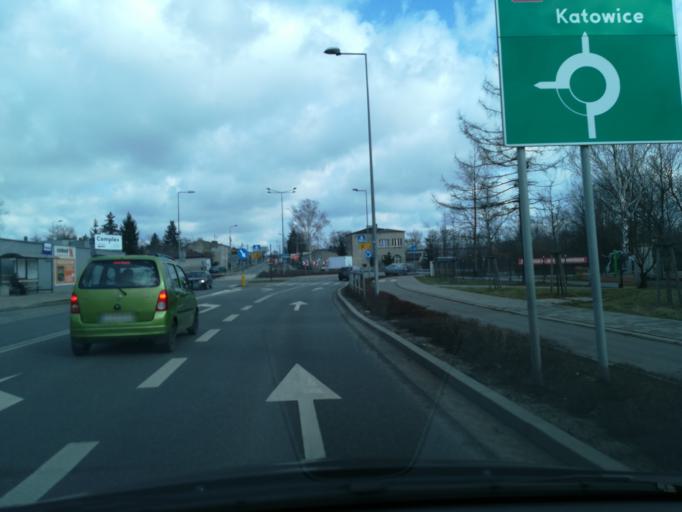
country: PL
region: Silesian Voivodeship
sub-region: Czestochowa
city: Czestochowa
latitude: 50.8232
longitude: 19.1335
